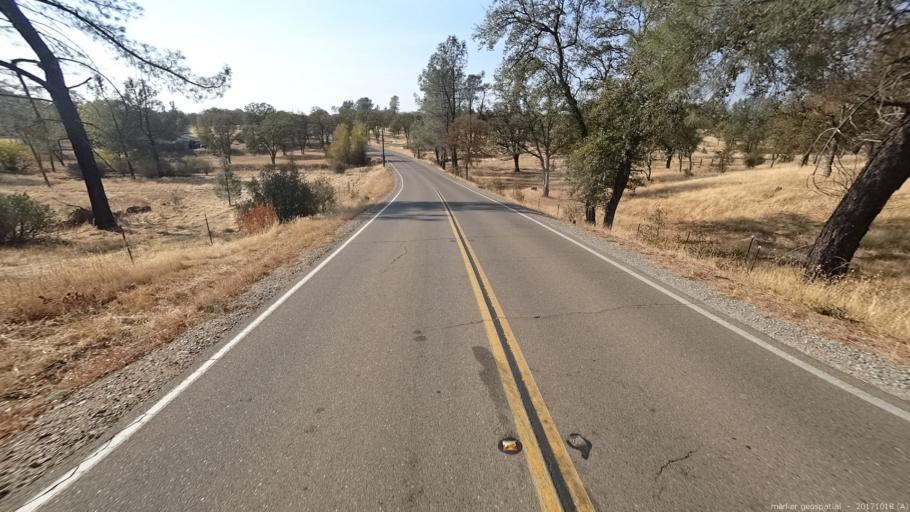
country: US
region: California
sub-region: Shasta County
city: Palo Cedro
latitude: 40.5639
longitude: -122.2733
